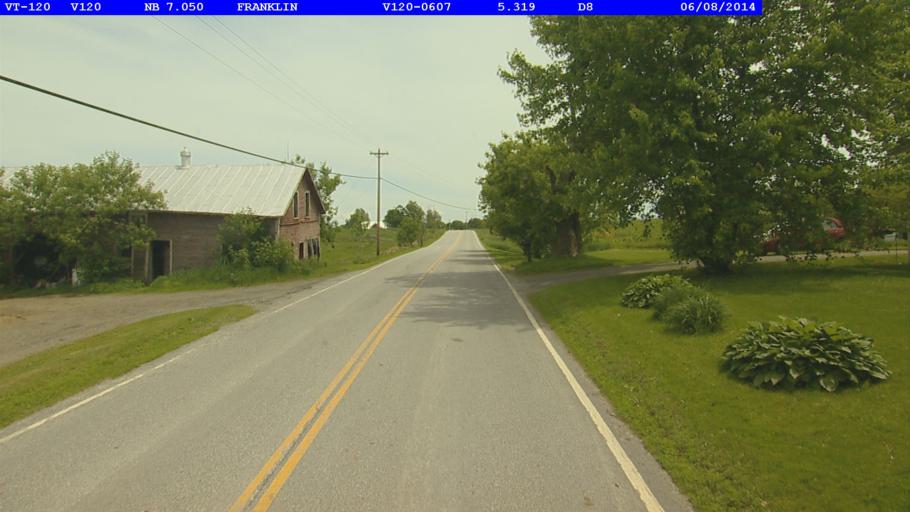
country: US
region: Vermont
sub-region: Franklin County
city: Enosburg Falls
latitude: 44.9863
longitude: -72.8869
